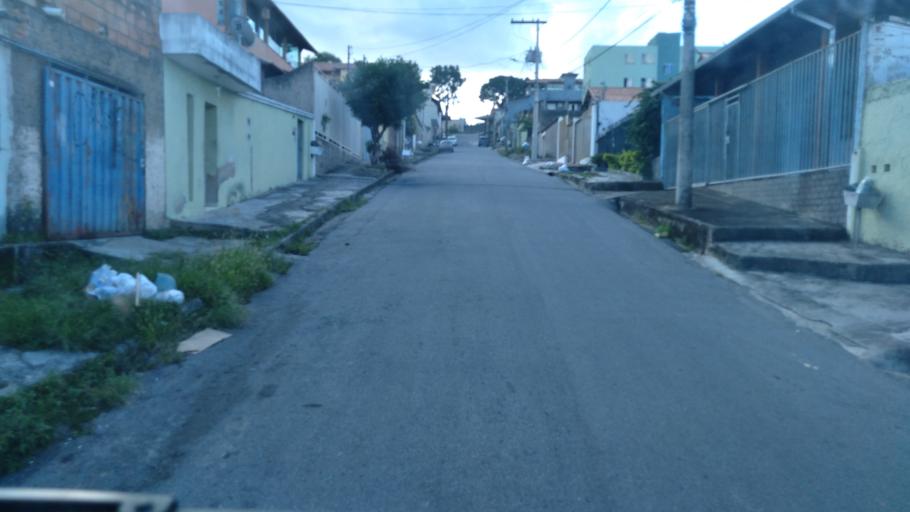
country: BR
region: Minas Gerais
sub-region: Belo Horizonte
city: Belo Horizonte
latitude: -19.8524
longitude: -43.9090
